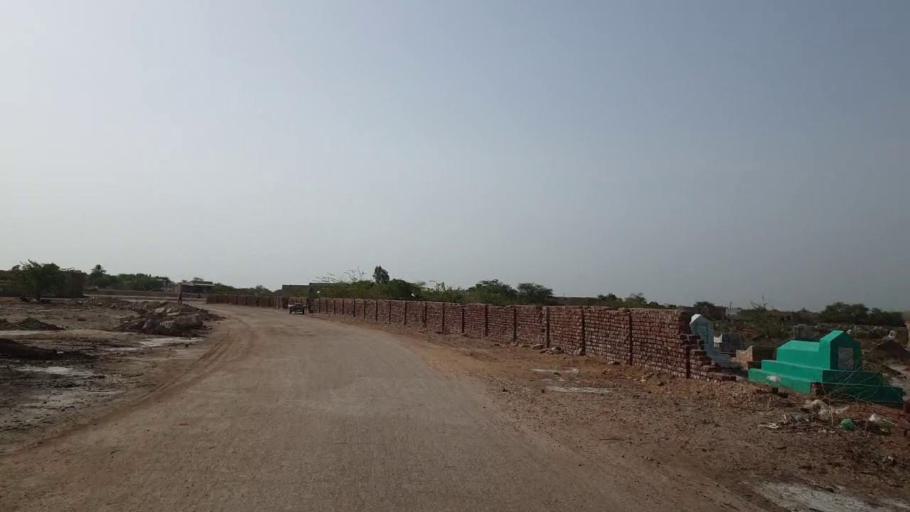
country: PK
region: Sindh
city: Jam Sahib
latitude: 26.2980
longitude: 68.6342
